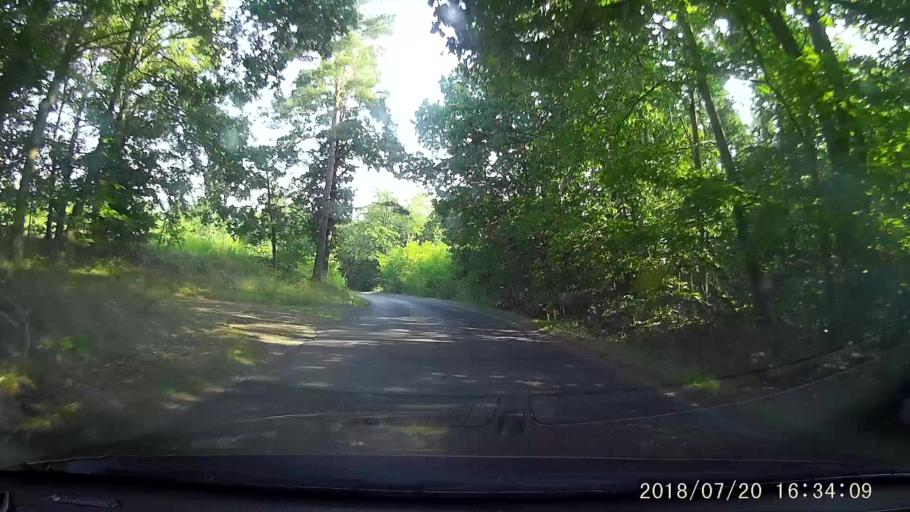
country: PL
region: Lower Silesian Voivodeship
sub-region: Powiat zgorzelecki
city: Sulikow
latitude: 51.0840
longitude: 15.0980
